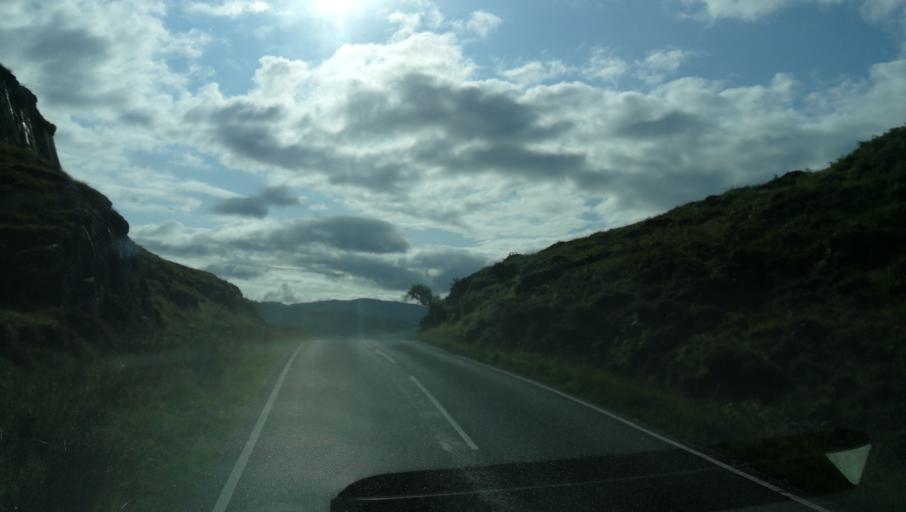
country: GB
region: Scotland
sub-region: Argyll and Bute
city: Isle Of Mull
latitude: 56.6789
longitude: -5.8480
